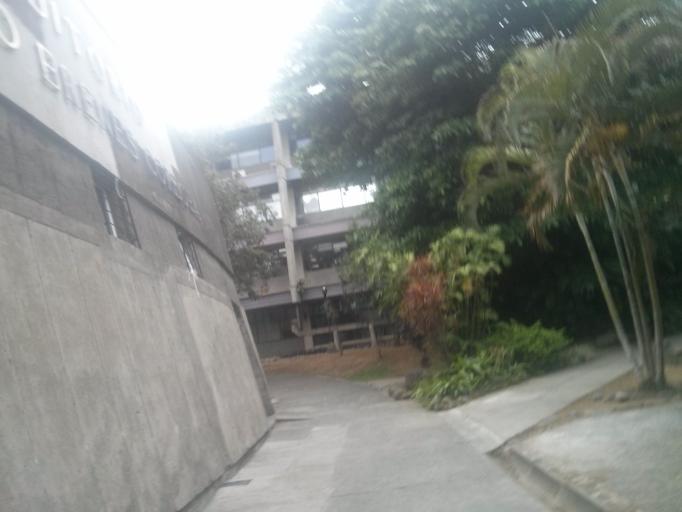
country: CR
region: San Jose
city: San Pedro
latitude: 9.9360
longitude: -84.0540
